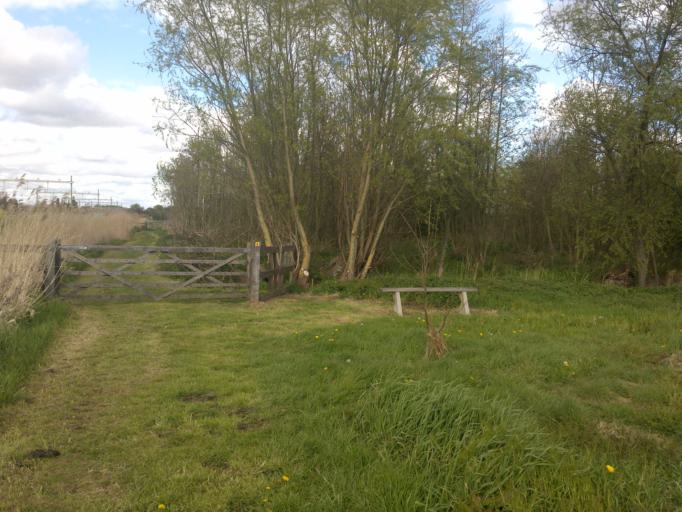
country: NL
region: South Holland
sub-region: Gemeente Lisse
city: Lisse
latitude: 52.2696
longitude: 4.5306
